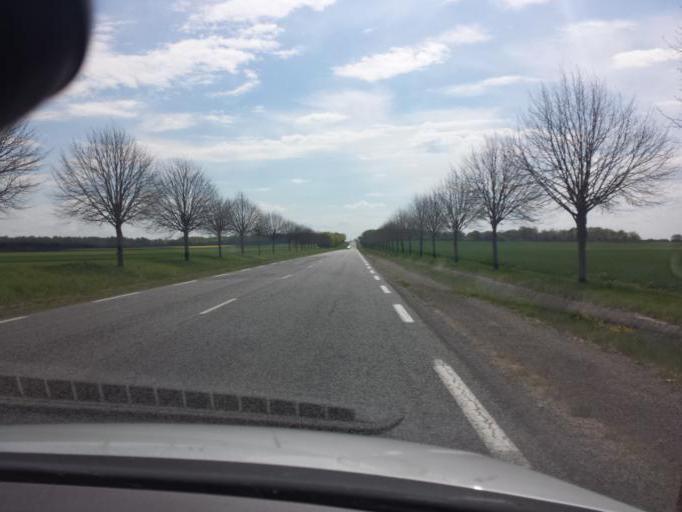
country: FR
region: Haute-Normandie
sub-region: Departement de l'Eure
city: Breteuil
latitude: 48.8295
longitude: 0.9340
